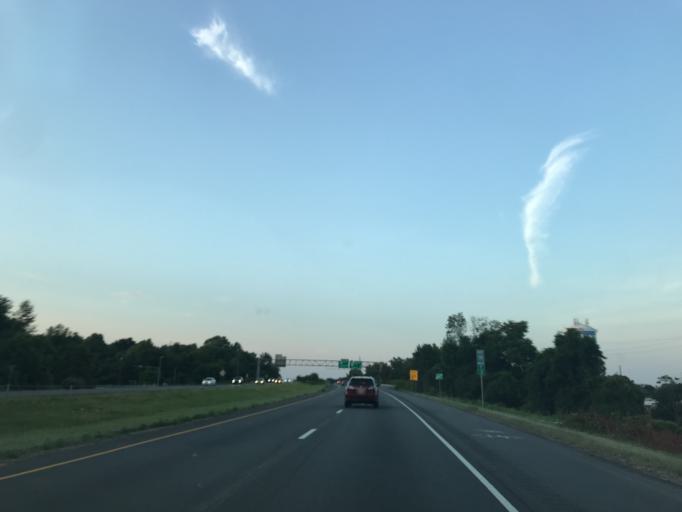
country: US
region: Pennsylvania
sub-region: Bucks County
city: Woodbourne
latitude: 40.1878
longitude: -74.8843
